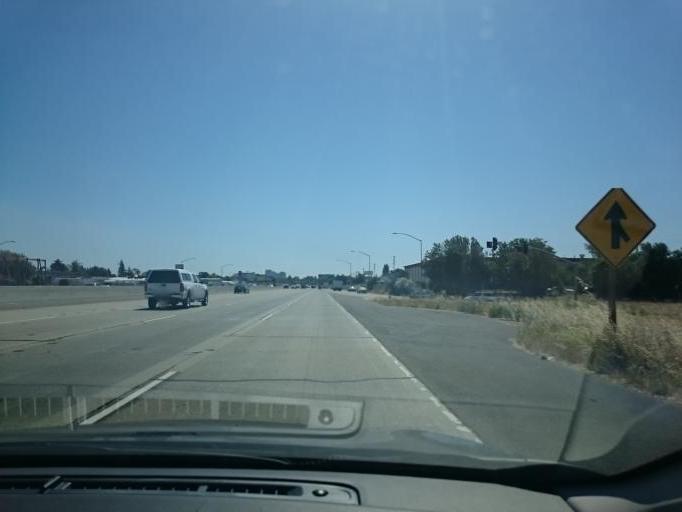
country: US
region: California
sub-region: Yolo County
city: West Sacramento
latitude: 38.5748
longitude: -121.5471
